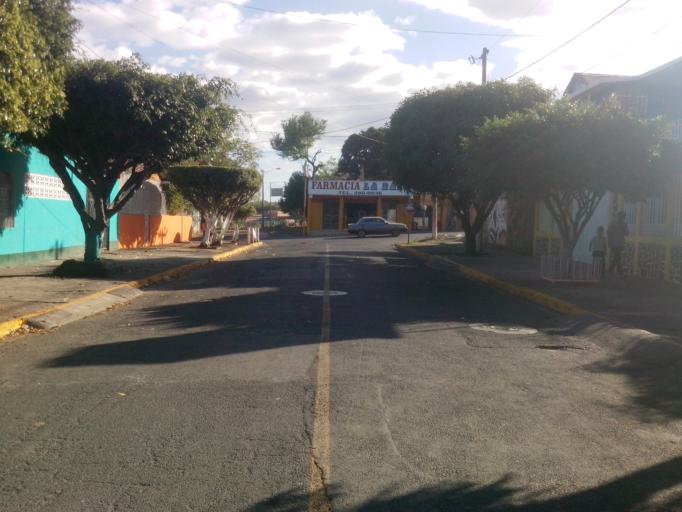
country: NI
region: Managua
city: Managua
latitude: 12.1195
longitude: -86.2049
